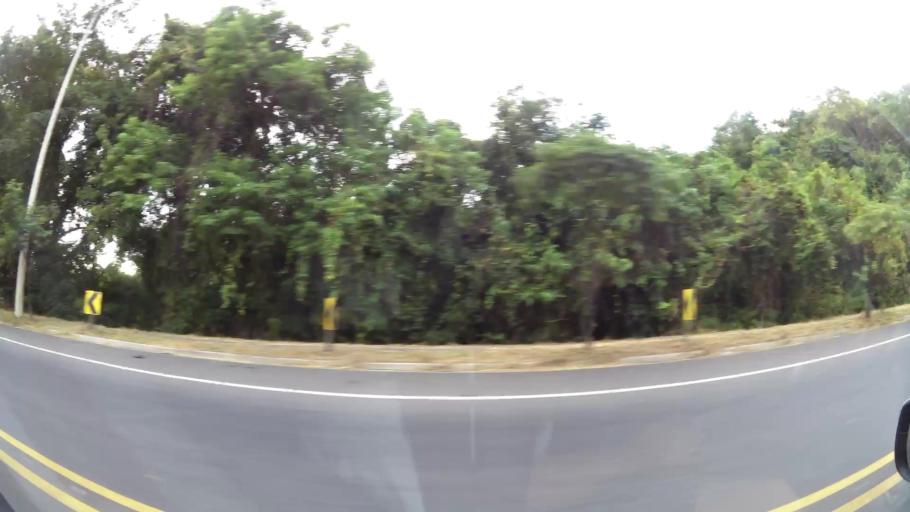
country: CR
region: Puntarenas
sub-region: Canton Central de Puntarenas
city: Chacarita
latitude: 9.9419
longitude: -84.7284
